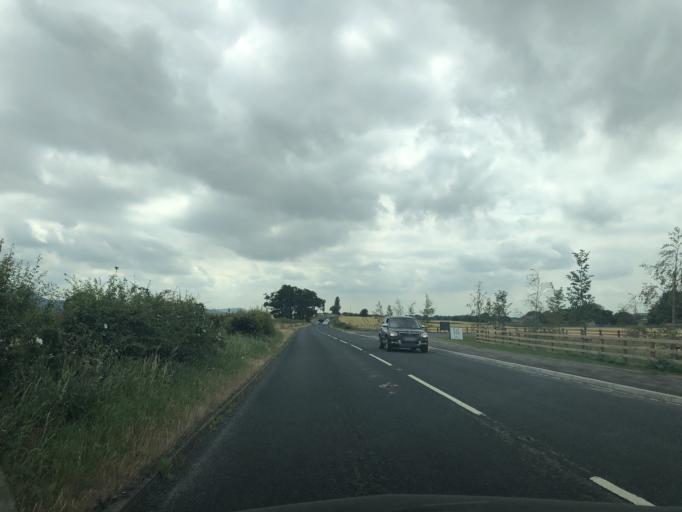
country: GB
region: England
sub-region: North Yorkshire
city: Great Ayton
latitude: 54.4797
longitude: -1.1522
